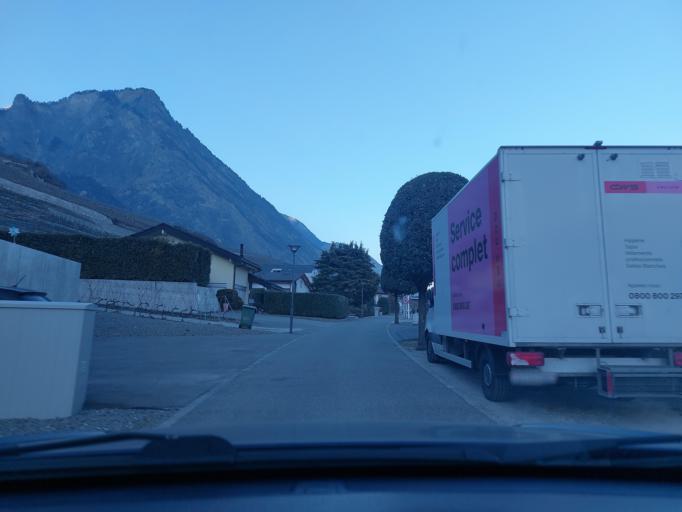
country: CH
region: Valais
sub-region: Martigny District
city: Saillon
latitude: 46.1771
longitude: 7.1908
